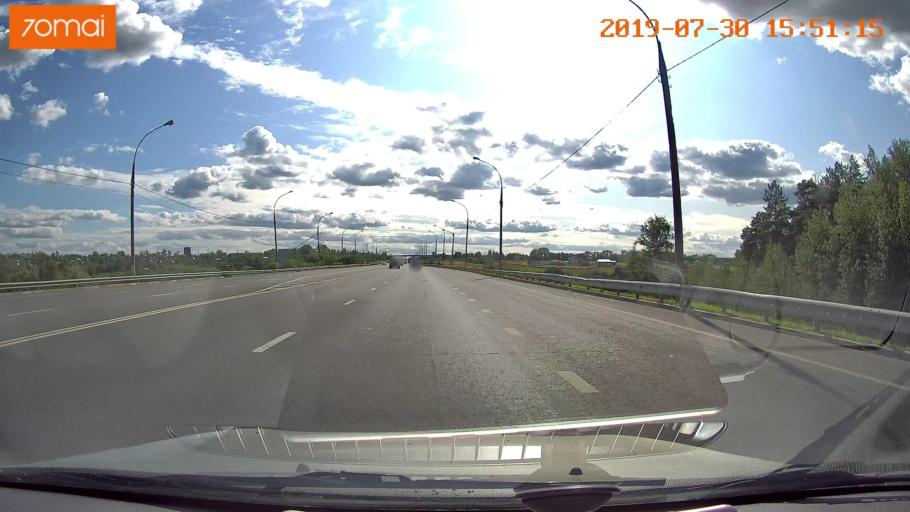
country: RU
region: Moskovskaya
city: Voskresensk
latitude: 55.3276
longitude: 38.6437
